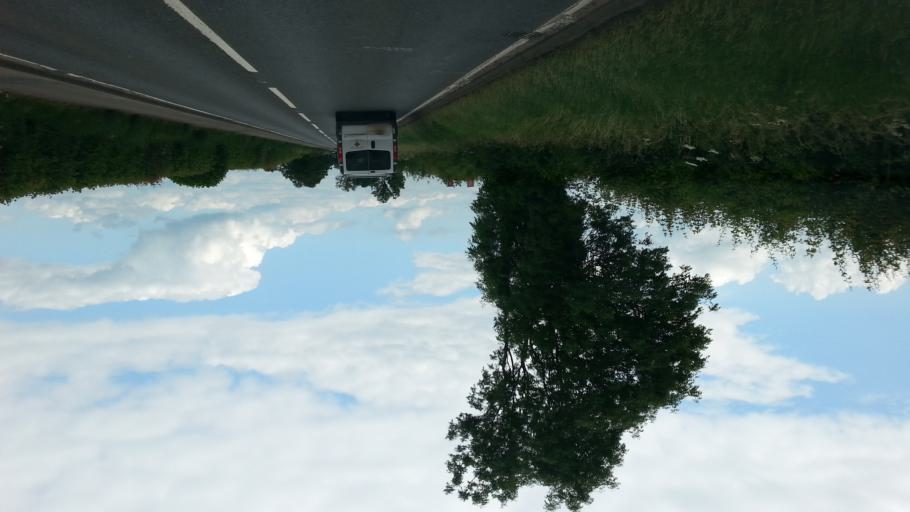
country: GB
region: England
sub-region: Worcestershire
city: Evesham
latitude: 52.0695
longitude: -1.9544
